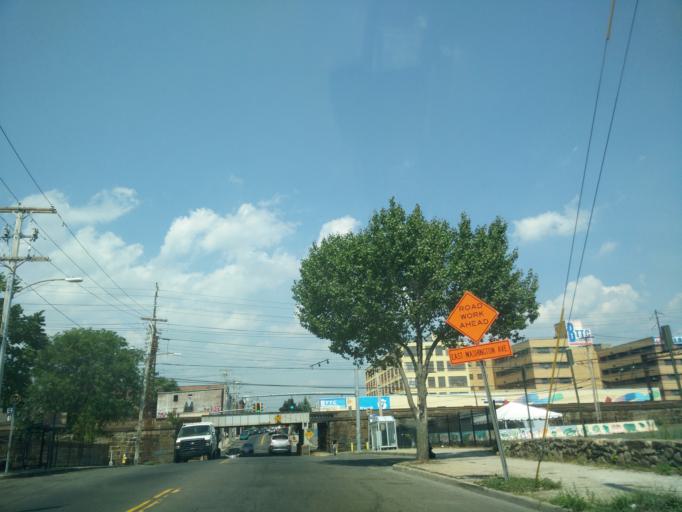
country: US
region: Connecticut
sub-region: Fairfield County
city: Bridgeport
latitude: 41.1850
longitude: -73.1809
